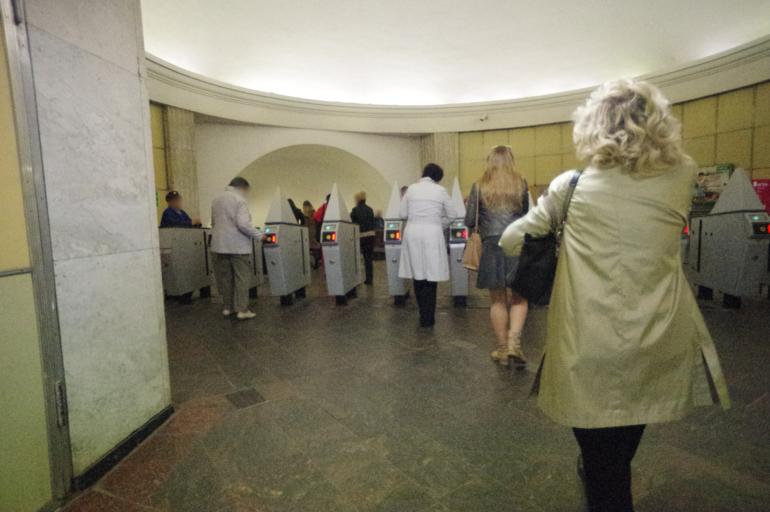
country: RU
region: Moskovskaya
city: Semenovskoye
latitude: 55.6917
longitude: 37.5349
